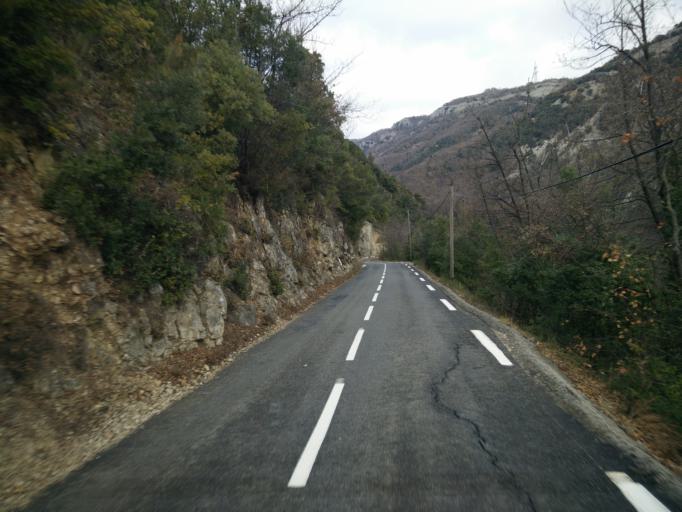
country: FR
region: Provence-Alpes-Cote d'Azur
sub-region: Departement des Alpes-Maritimes
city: Tourrettes-sur-Loup
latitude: 43.7554
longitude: 6.9892
